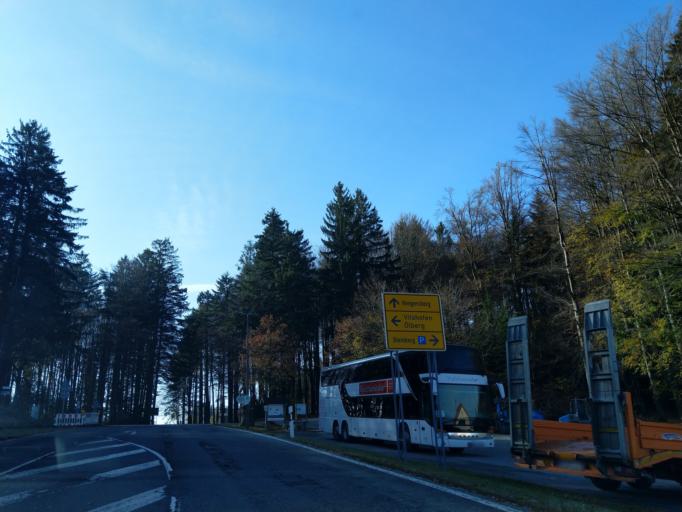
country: DE
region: Bavaria
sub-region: Lower Bavaria
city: Hunding
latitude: 48.8215
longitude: 13.1990
